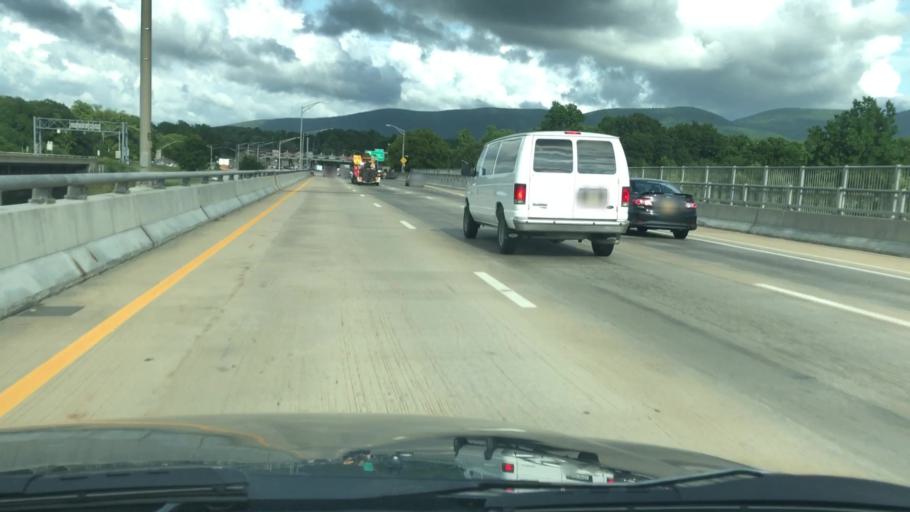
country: US
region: New York
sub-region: Dutchess County
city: Beacon
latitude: 41.5183
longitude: -73.9840
